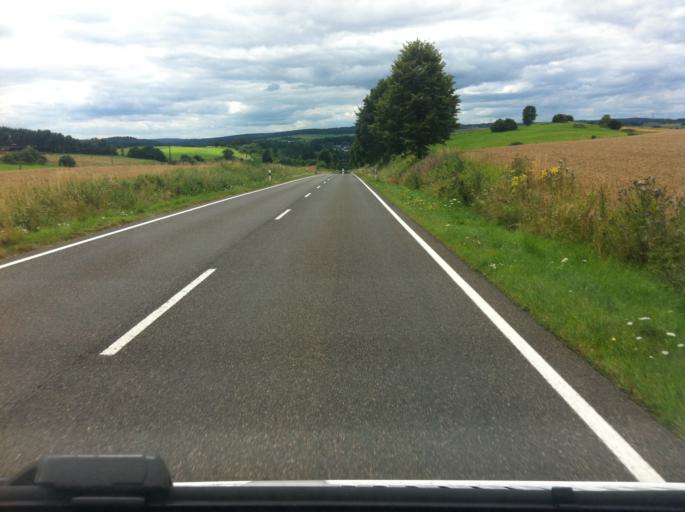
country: DE
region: North Rhine-Westphalia
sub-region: Regierungsbezirk Koln
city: Nettersheim
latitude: 50.5063
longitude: 6.6403
